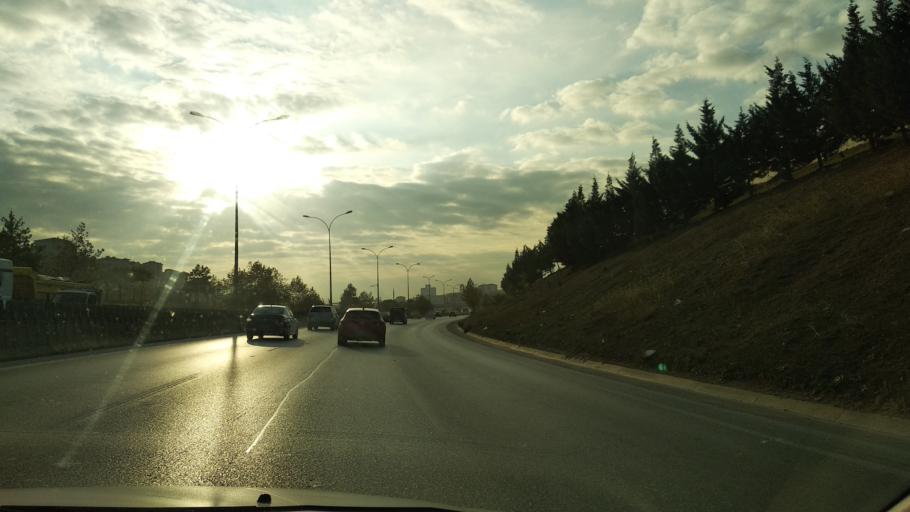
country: TR
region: Istanbul
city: Pendik
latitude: 40.8748
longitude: 29.3004
